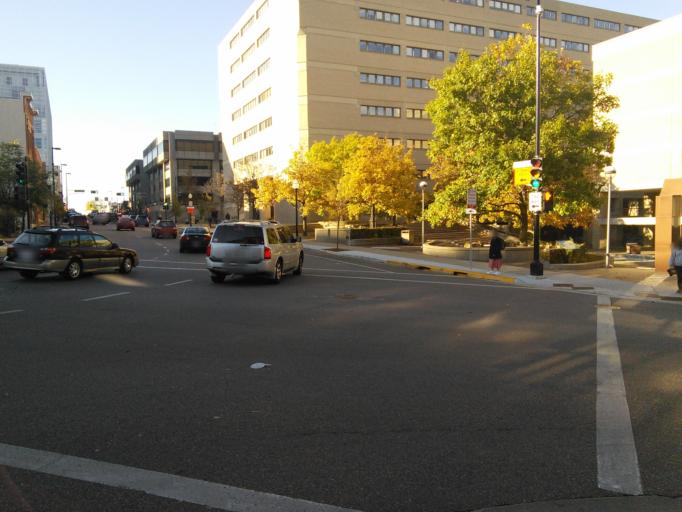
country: US
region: Wisconsin
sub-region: Dane County
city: Madison
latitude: 43.0751
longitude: -89.3802
